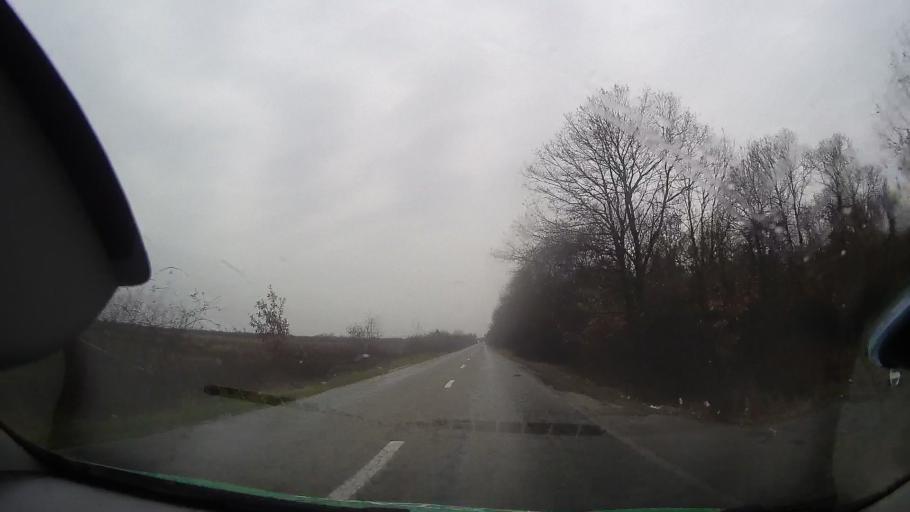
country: RO
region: Bihor
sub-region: Comuna Tinca
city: Gurbediu
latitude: 46.7901
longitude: 21.8341
